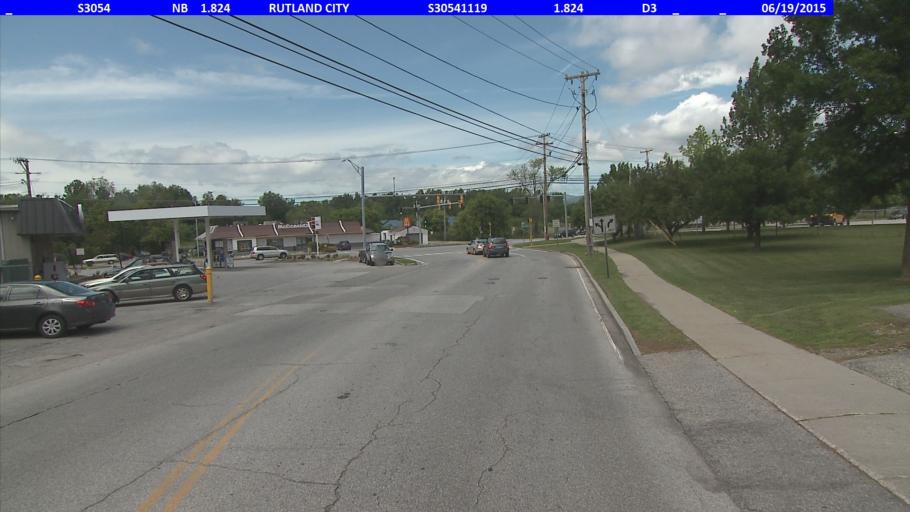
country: US
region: Vermont
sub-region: Rutland County
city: Rutland
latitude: 43.6174
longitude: -72.9568
